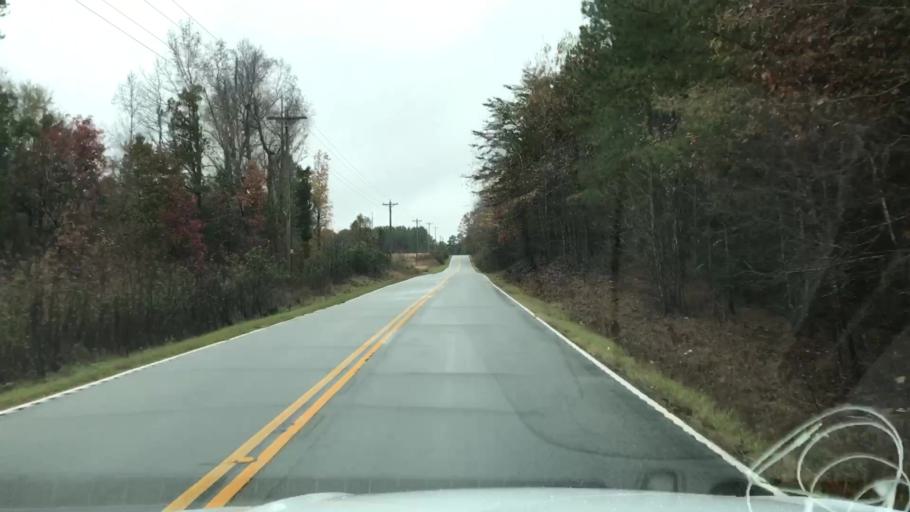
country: US
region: South Carolina
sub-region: Spartanburg County
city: Roebuck
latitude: 34.7704
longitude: -81.9115
